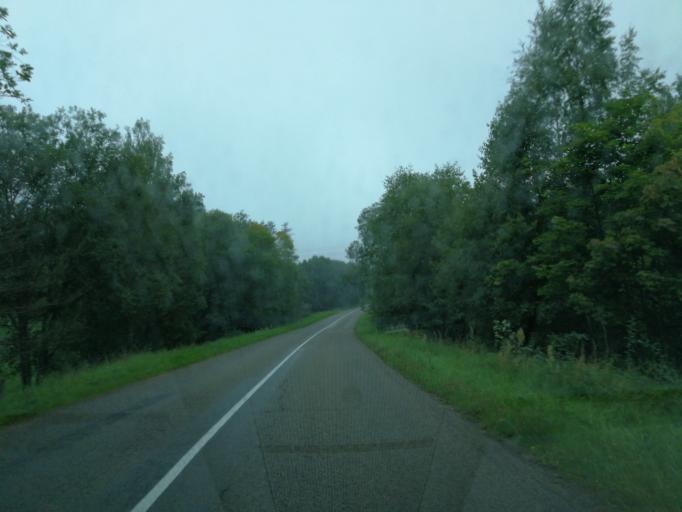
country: LV
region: Preilu Rajons
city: Jaunaglona
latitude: 56.2614
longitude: 27.0152
